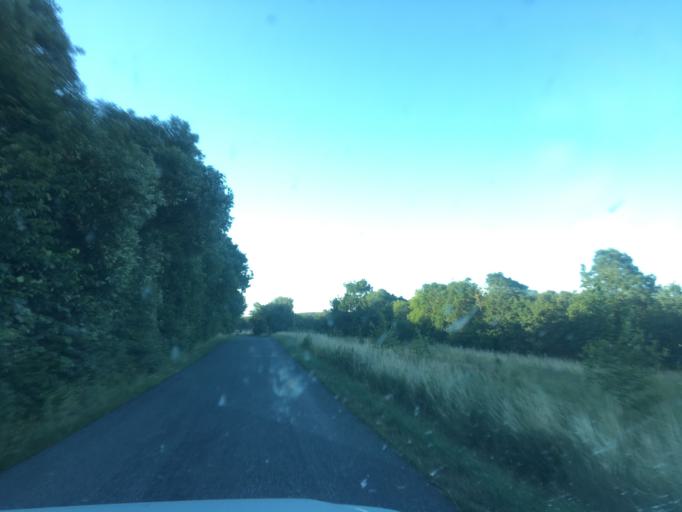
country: DK
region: Central Jutland
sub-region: Randers Kommune
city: Langa
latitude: 56.3909
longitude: 9.8599
